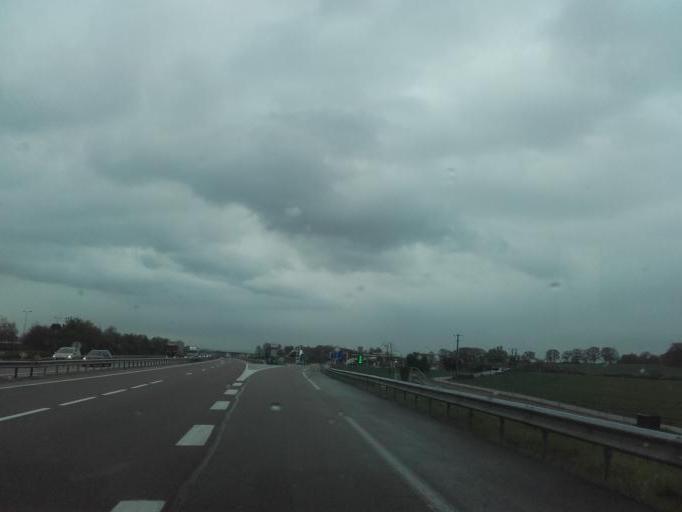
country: FR
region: Bourgogne
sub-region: Departement de l'Yonne
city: Avallon
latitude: 47.5035
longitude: 4.0314
